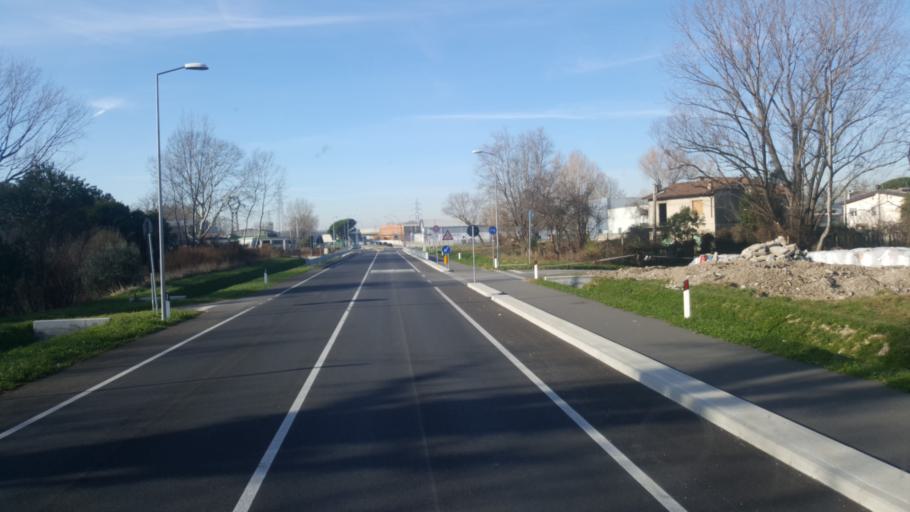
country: IT
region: Friuli Venezia Giulia
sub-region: Provincia di Gorizia
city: Monfalcone
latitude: 45.7917
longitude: 13.5276
